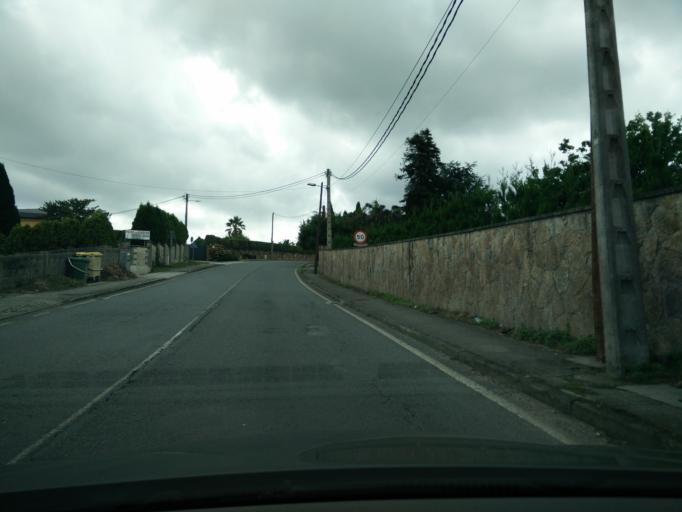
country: ES
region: Galicia
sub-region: Provincia da Coruna
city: Culleredo
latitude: 43.3275
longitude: -8.4035
